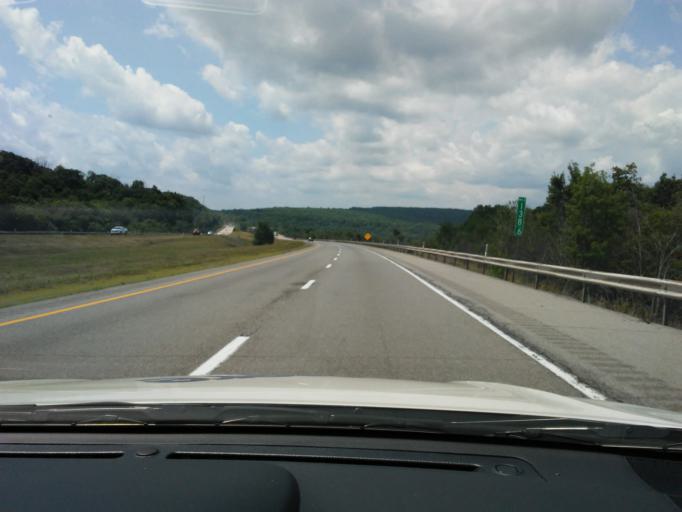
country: US
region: Pennsylvania
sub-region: Clearfield County
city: Troy
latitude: 40.9701
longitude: -78.0757
